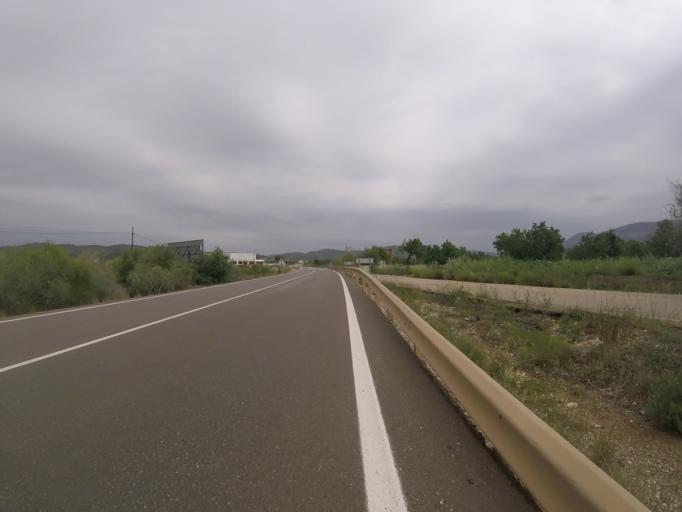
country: ES
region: Valencia
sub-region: Provincia de Castello
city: Alcoceber
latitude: 40.2542
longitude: 0.2458
